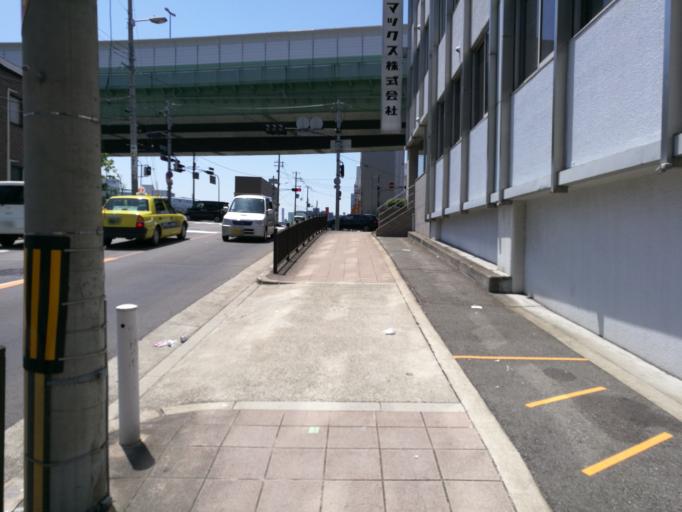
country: JP
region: Osaka
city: Osaka-shi
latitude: 34.6876
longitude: 135.4824
